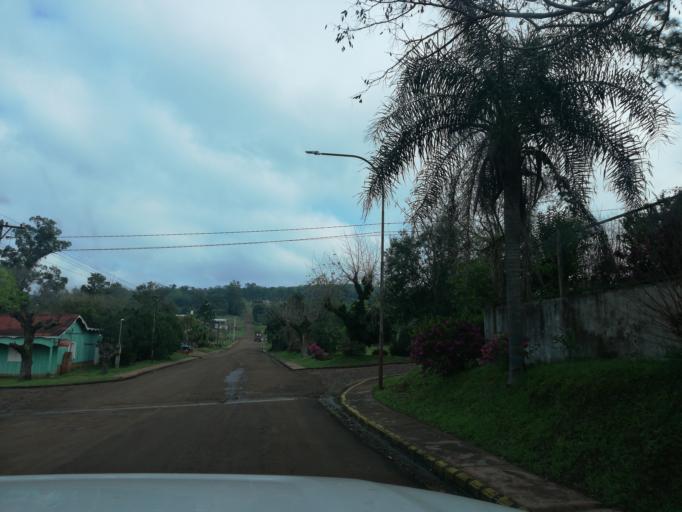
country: AR
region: Misiones
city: Cerro Azul
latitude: -27.5679
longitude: -55.5029
